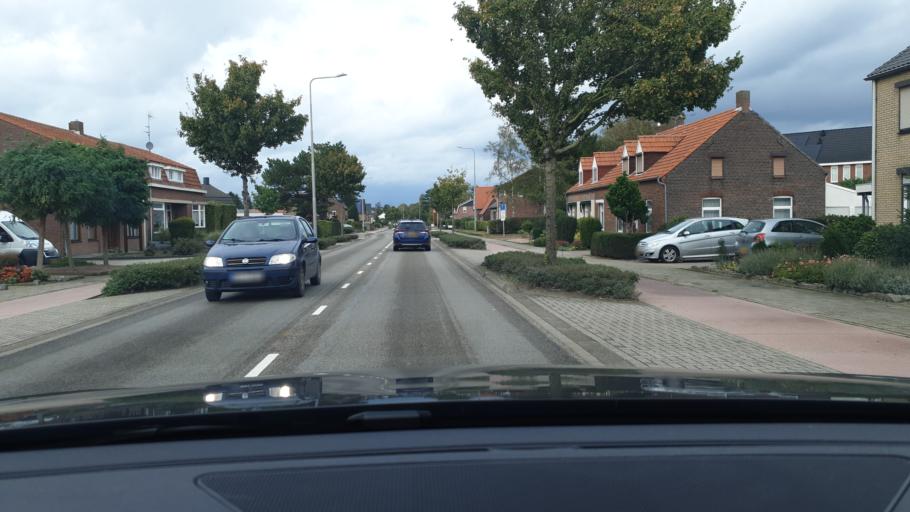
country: NL
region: Limburg
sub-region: Gemeente Venlo
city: Venlo
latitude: 51.4179
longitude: 6.1667
